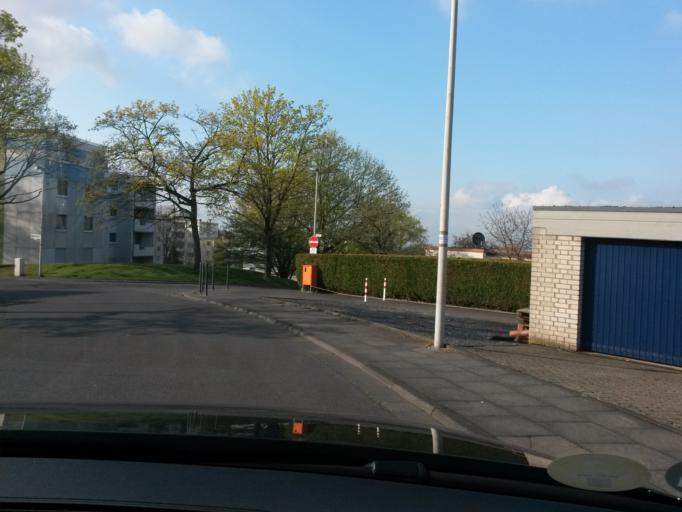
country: DE
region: North Rhine-Westphalia
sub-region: Regierungsbezirk Koln
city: Alfter
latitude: 50.7096
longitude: 7.0367
